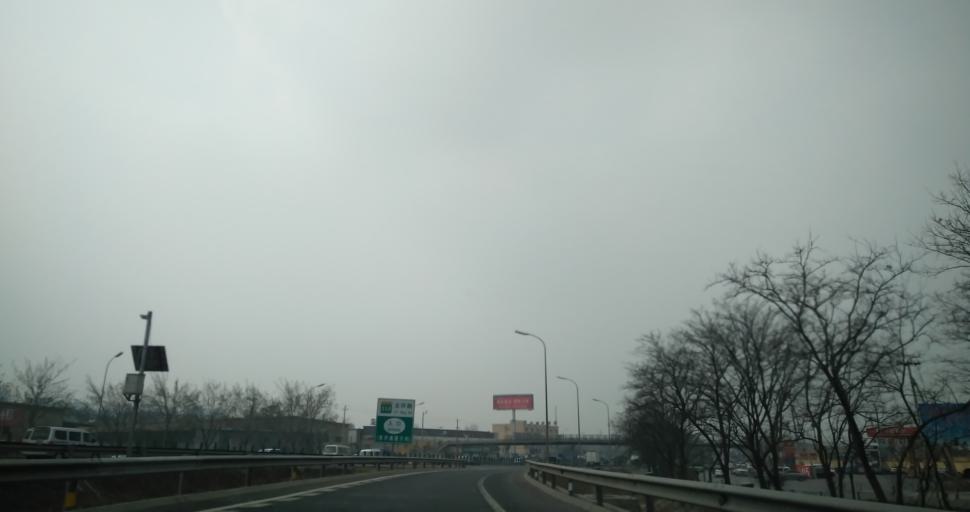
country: CN
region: Beijing
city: Jiugong
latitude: 39.8177
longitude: 116.4955
